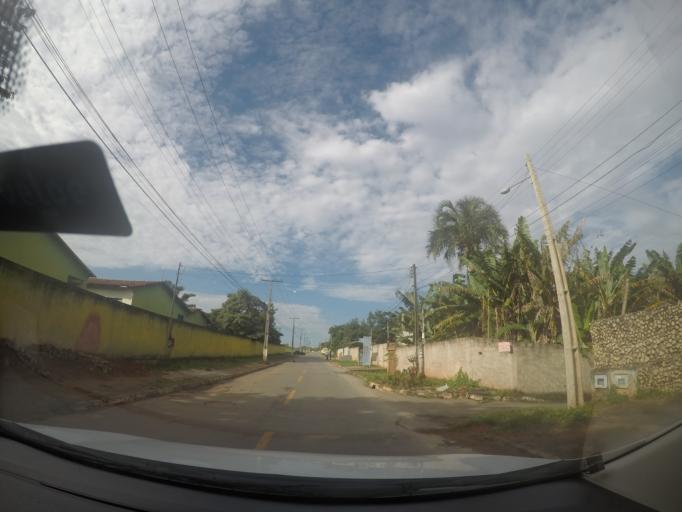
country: BR
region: Goias
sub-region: Goiania
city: Goiania
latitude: -16.6879
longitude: -49.1890
